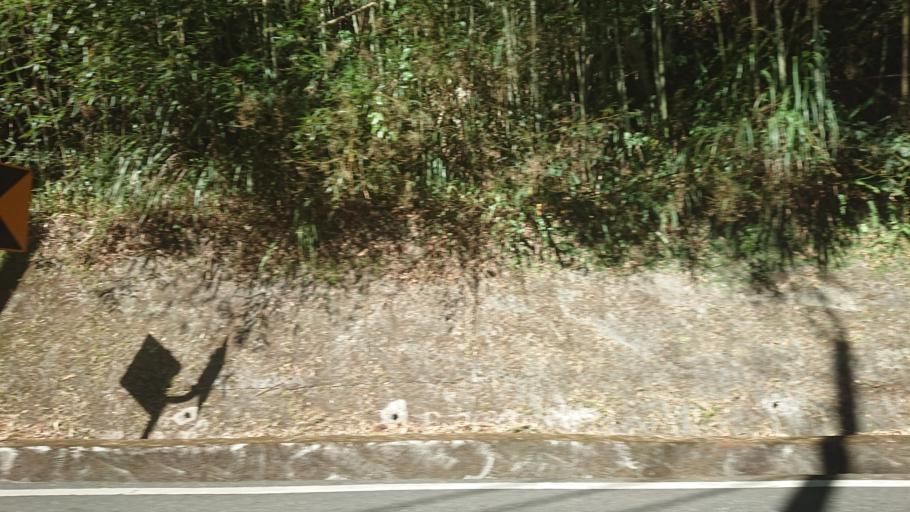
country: TW
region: Taiwan
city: Lugu
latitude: 23.4898
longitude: 120.7530
